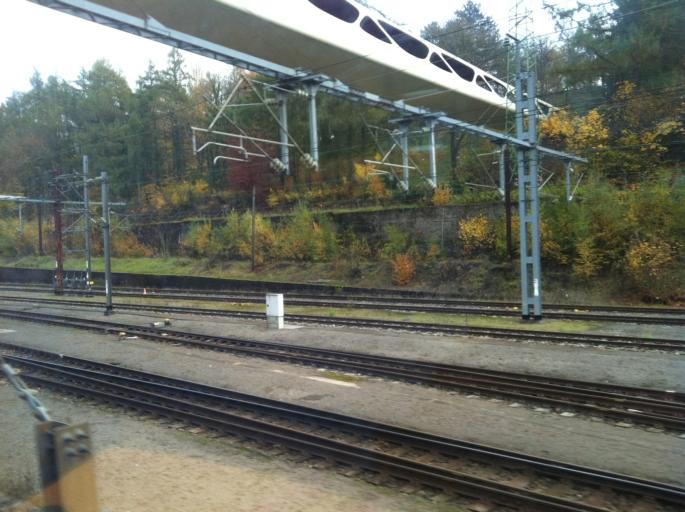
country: LU
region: Luxembourg
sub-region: Canton d'Esch-sur-Alzette
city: Esch-sur-Alzette
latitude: 49.4931
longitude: 5.9845
